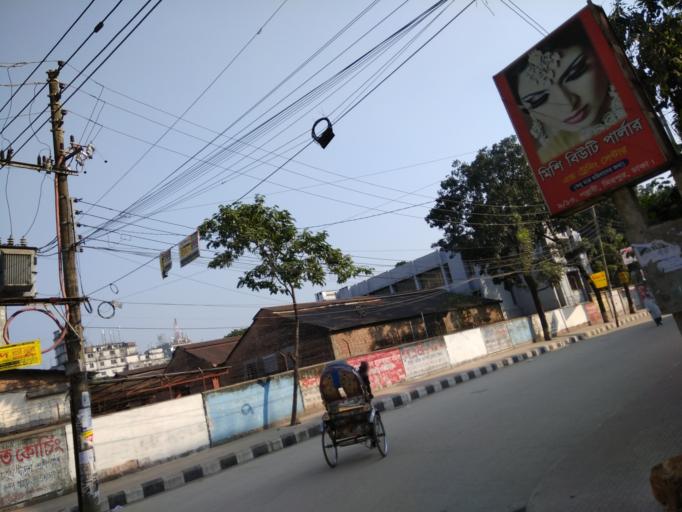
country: BD
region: Dhaka
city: Tungi
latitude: 23.8254
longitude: 90.3619
